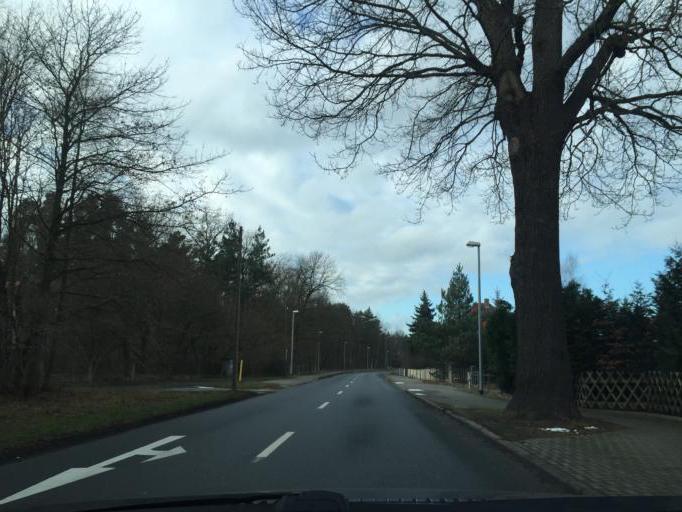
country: DE
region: Saxony
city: Ottendorf-Okrilla
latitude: 51.1729
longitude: 13.8336
